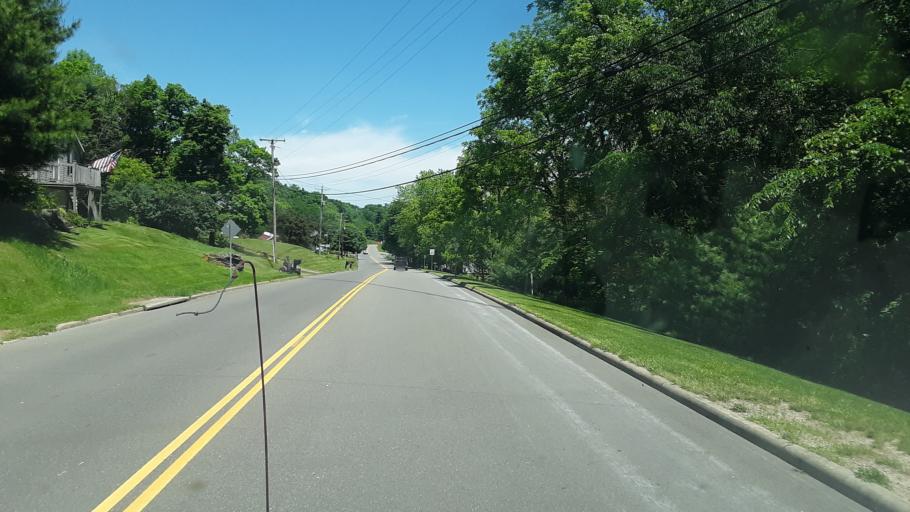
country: US
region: Ohio
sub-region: Coshocton County
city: Coshocton
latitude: 40.2729
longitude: -81.8908
